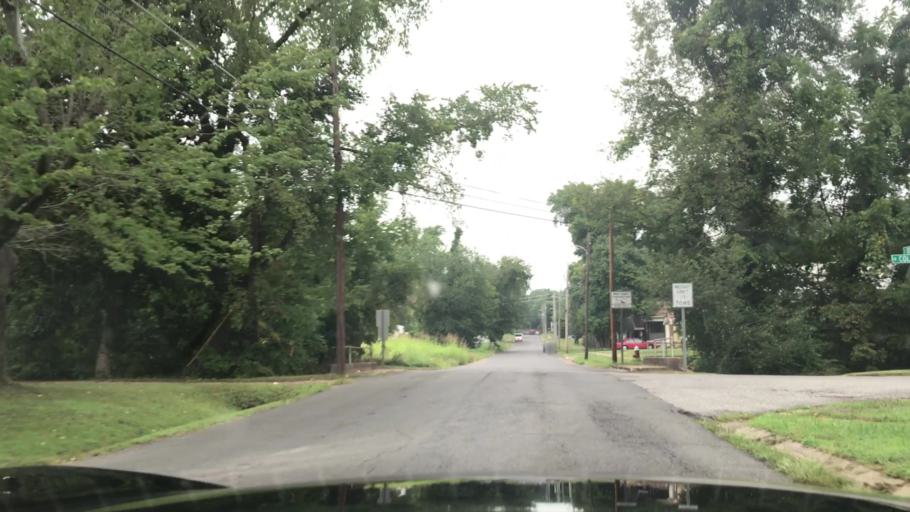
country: US
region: Kentucky
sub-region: Graves County
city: Mayfield
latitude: 36.7342
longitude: -88.6410
